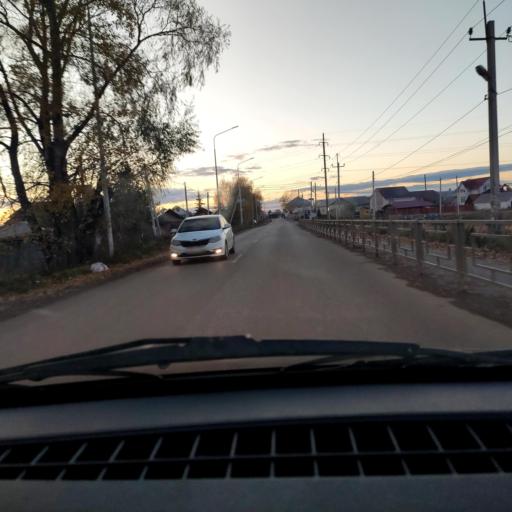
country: RU
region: Bashkortostan
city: Ufa
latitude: 54.6378
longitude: 55.9256
